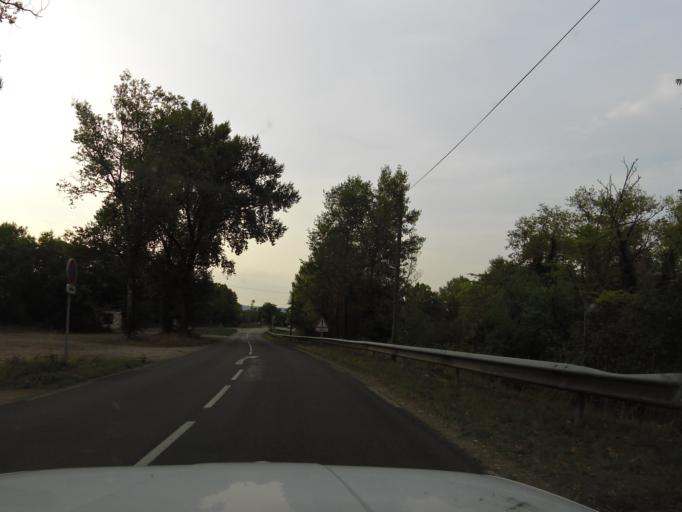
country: FR
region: Rhone-Alpes
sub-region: Departement de l'Ain
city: Saint-Jean-de-Niost
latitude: 45.8155
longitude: 5.2132
